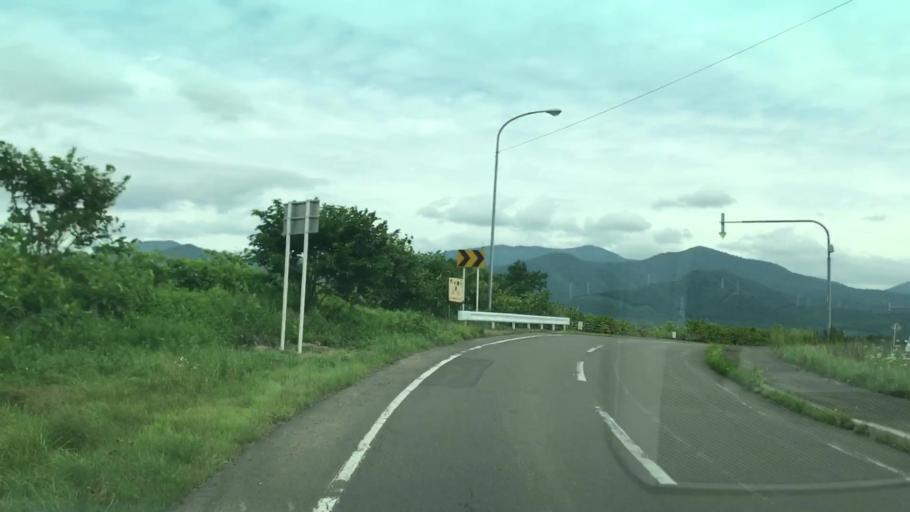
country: JP
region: Hokkaido
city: Iwanai
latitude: 43.0174
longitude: 140.5685
